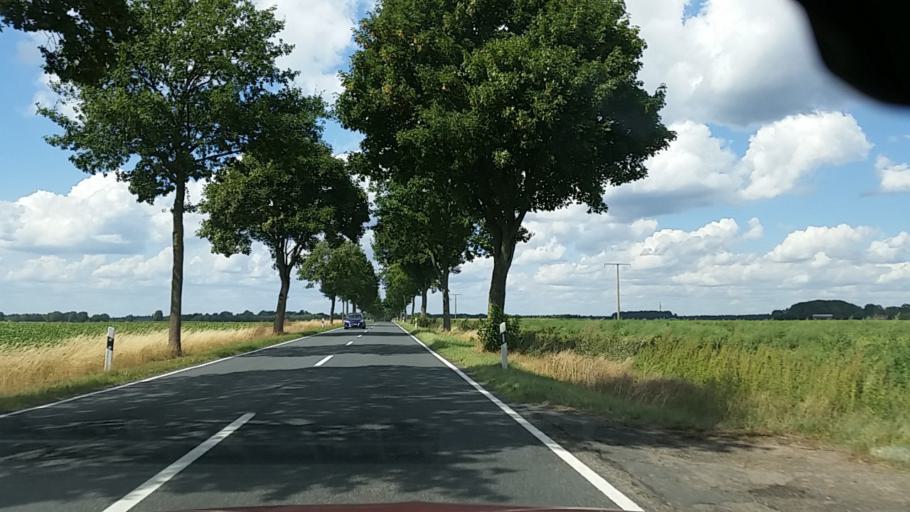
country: DE
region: Lower Saxony
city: Sprakensehl
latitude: 52.7559
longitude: 10.5098
